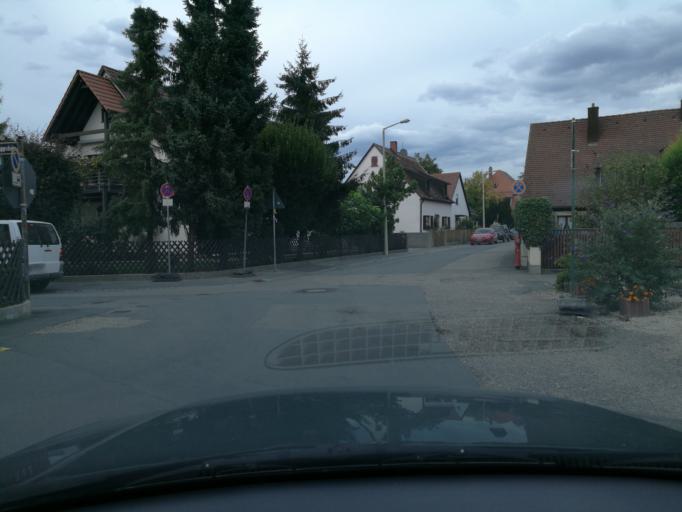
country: DE
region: Bavaria
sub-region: Regierungsbezirk Mittelfranken
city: Wetzendorf
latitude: 49.5102
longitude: 11.0483
